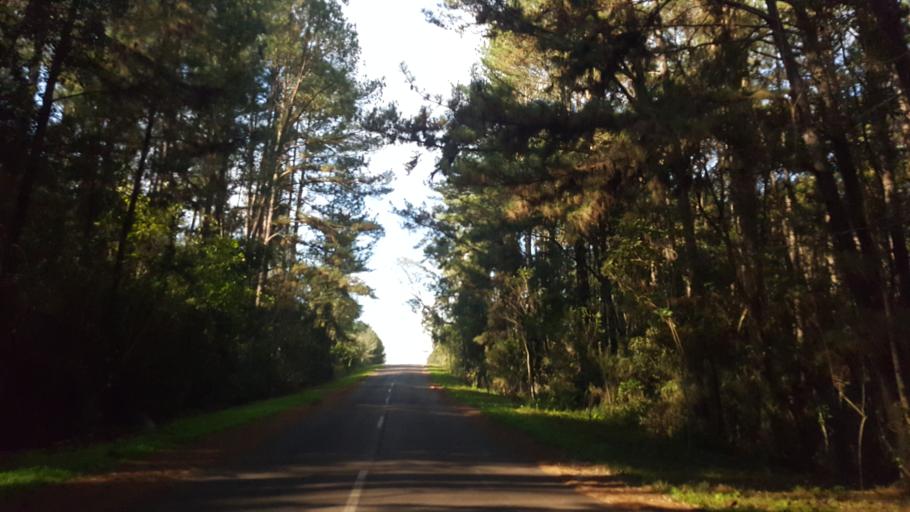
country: AR
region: Misiones
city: Puerto Leoni
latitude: -27.0039
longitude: -55.1864
